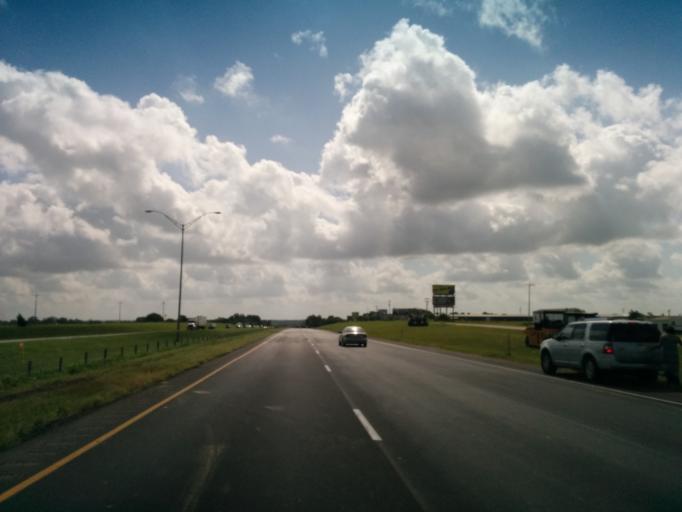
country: US
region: Texas
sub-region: Fayette County
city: Schulenburg
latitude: 29.6942
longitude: -96.8971
